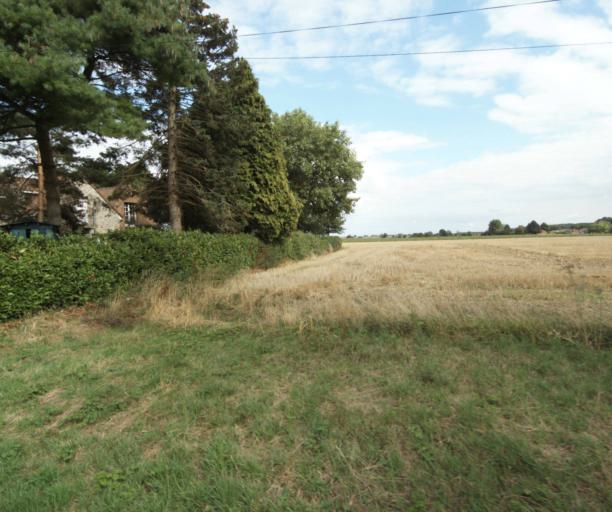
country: FR
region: Nord-Pas-de-Calais
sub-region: Departement du Nord
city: Sainghin-en-Melantois
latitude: 50.5942
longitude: 3.1713
